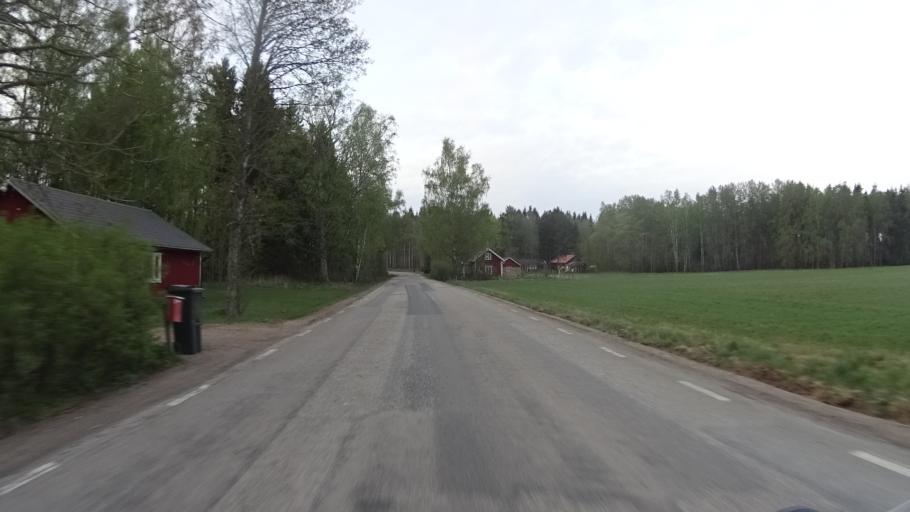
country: SE
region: Vaestra Goetaland
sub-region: Gotene Kommun
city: Kallby
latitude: 58.4872
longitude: 13.3147
